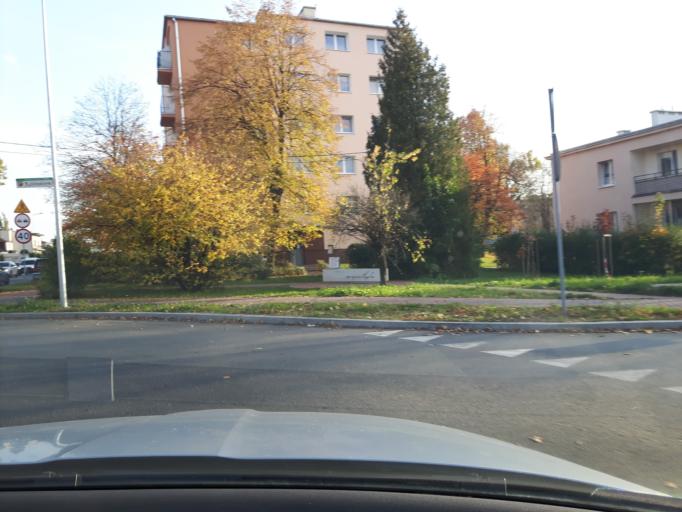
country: PL
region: Masovian Voivodeship
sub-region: Powiat wolominski
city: Zabki
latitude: 52.2954
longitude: 21.1121
